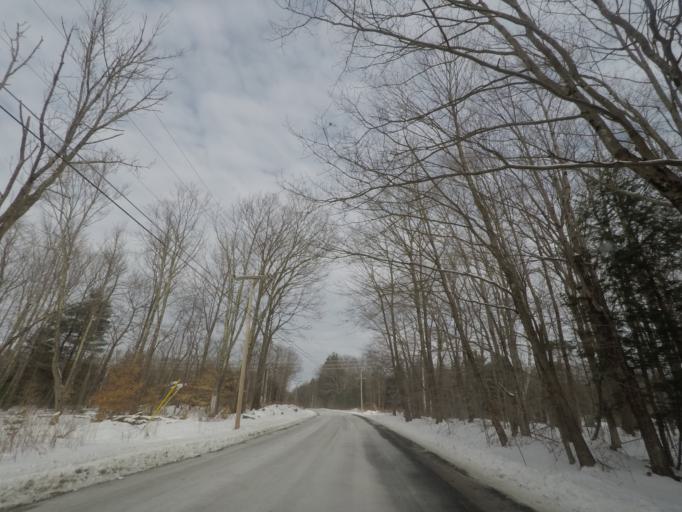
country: US
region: New York
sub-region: Rensselaer County
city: Averill Park
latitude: 42.5919
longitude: -73.4849
